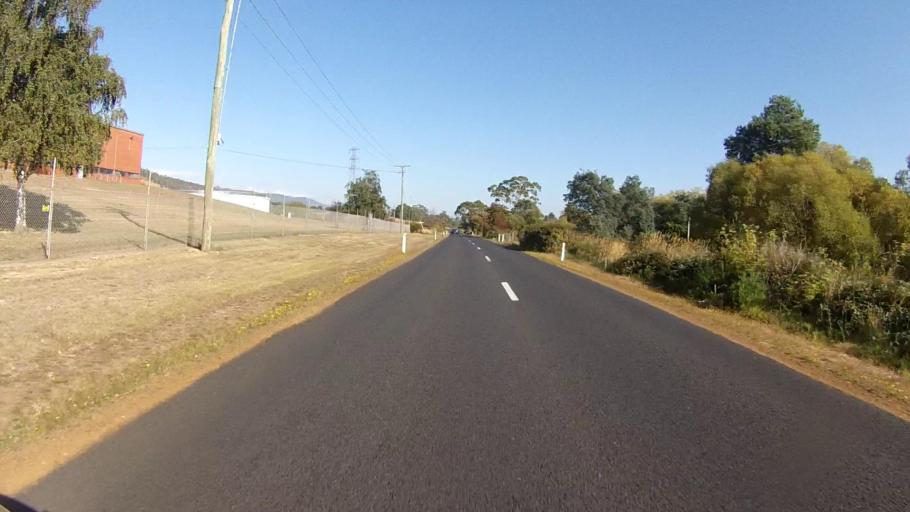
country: AU
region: Tasmania
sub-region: Derwent Valley
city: New Norfolk
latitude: -42.7677
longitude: 147.0226
